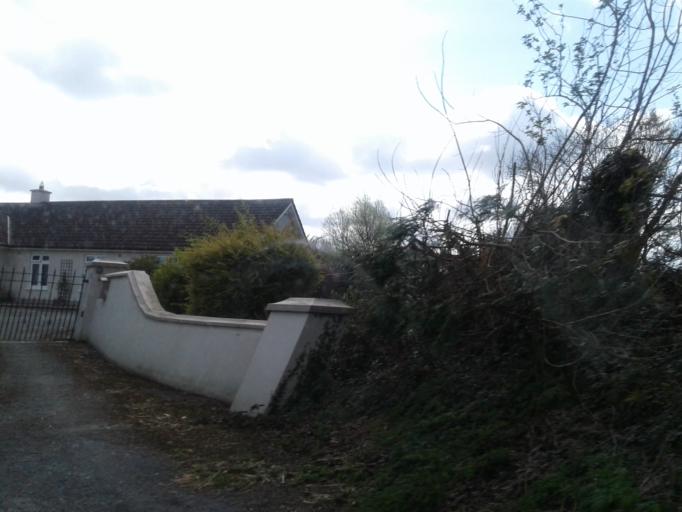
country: IE
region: Leinster
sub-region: An Mhi
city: Ashbourne
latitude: 53.4915
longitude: -6.3553
